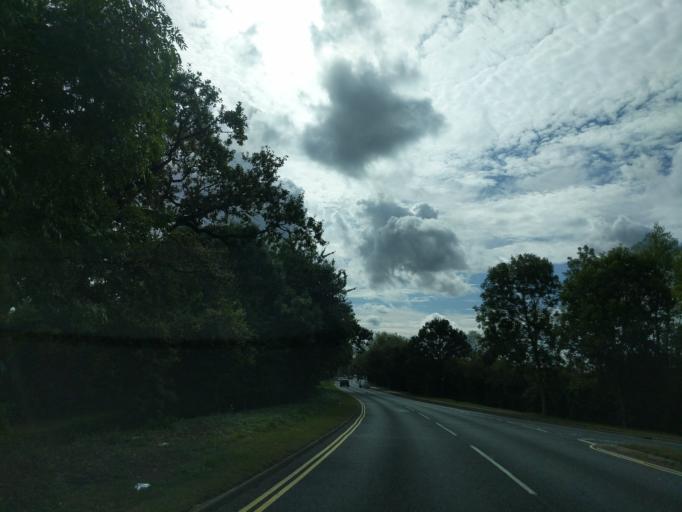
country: GB
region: England
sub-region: Oxfordshire
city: Oxford
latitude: 51.7736
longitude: -1.2297
